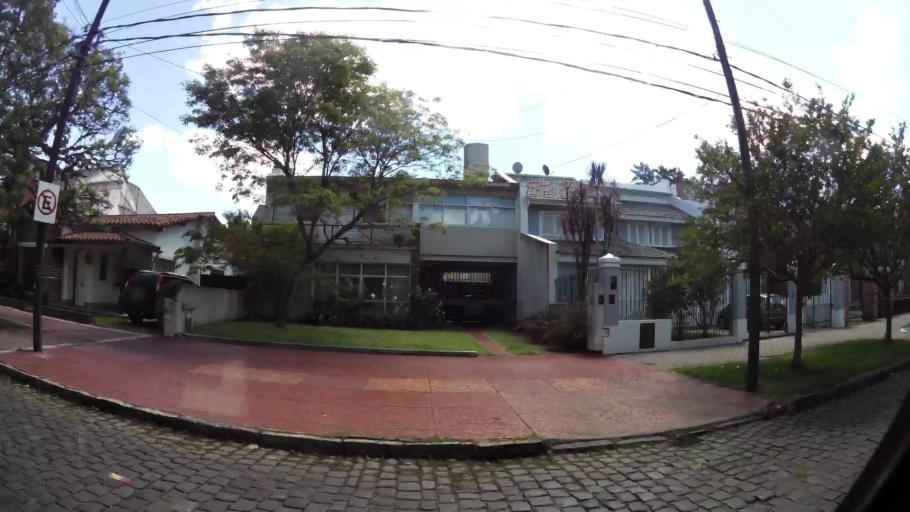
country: AR
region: Buenos Aires
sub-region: Partido de Lomas de Zamora
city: Lomas de Zamora
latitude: -34.7413
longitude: -58.4046
